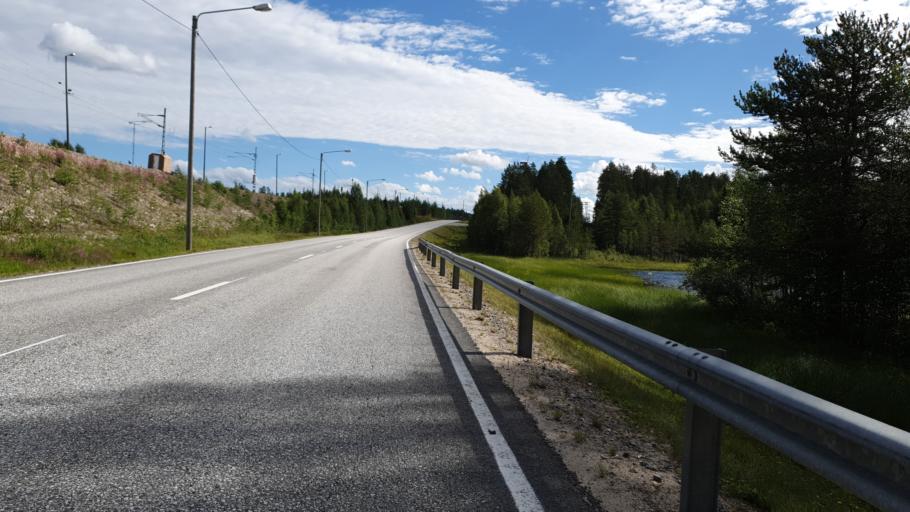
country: FI
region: Kainuu
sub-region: Kehys-Kainuu
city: Kuhmo
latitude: 64.5430
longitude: 29.9674
